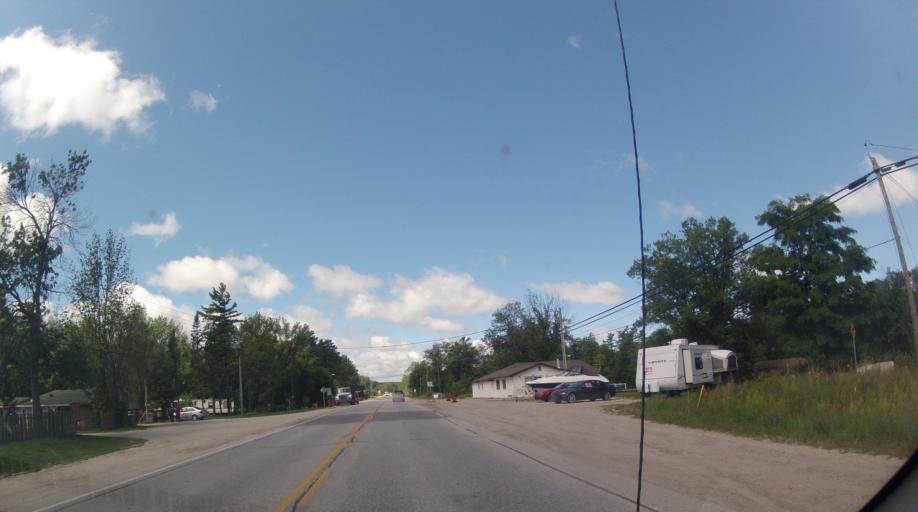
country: CA
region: Ontario
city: Collingwood
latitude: 44.4682
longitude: -80.1127
